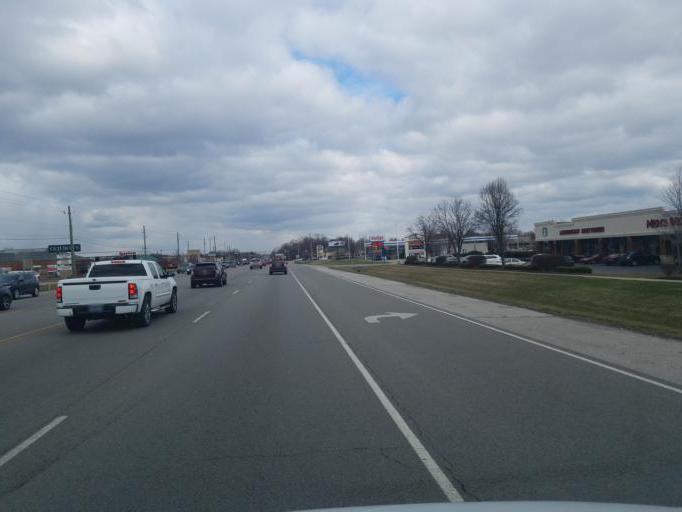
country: US
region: Indiana
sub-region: Marion County
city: Clermont
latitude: 39.7636
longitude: -86.3305
